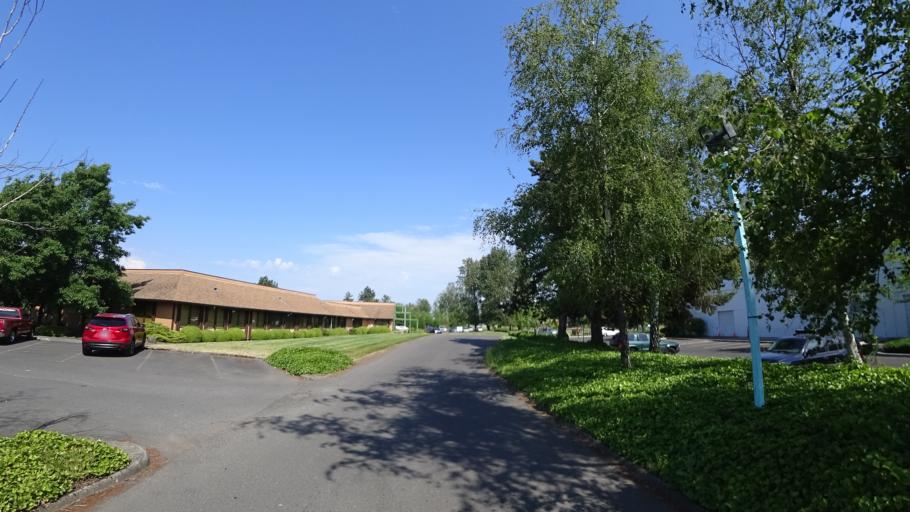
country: US
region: Oregon
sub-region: Multnomah County
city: Fairview
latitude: 45.5571
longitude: -122.5150
